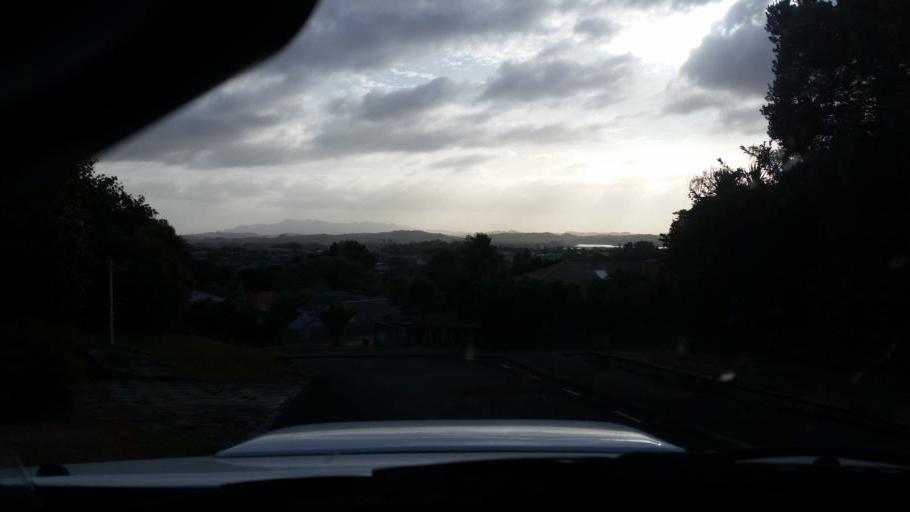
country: NZ
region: Northland
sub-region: Kaipara District
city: Dargaville
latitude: -35.9318
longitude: 173.8546
